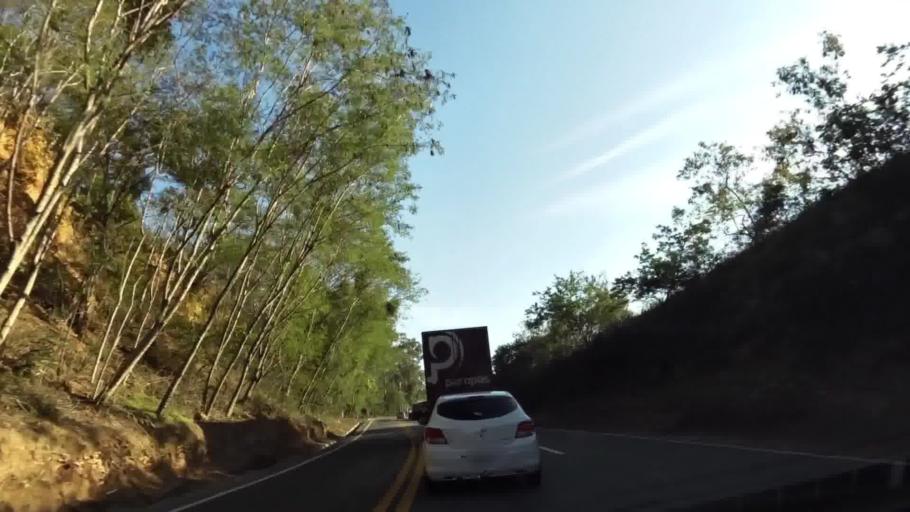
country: BR
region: Espirito Santo
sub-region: Viana
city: Viana
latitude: -20.4777
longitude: -40.4711
